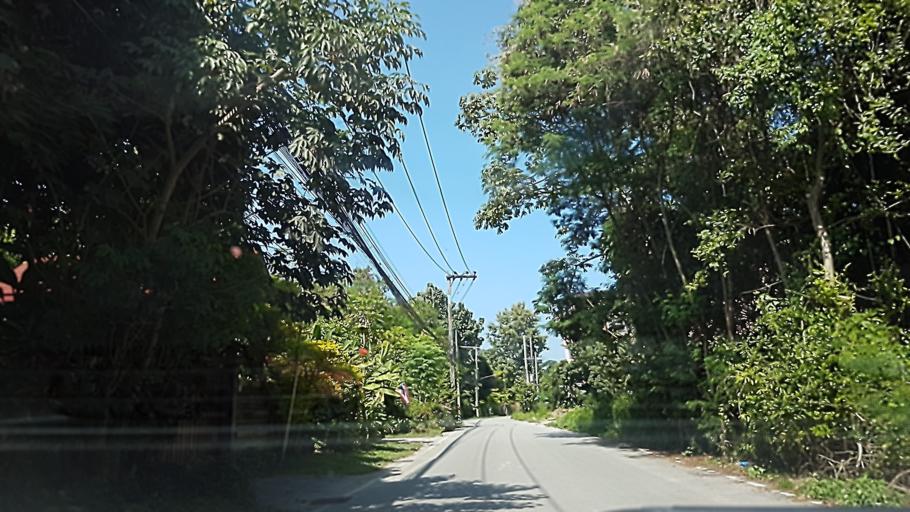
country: TH
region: Chiang Mai
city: Chiang Mai
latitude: 18.8205
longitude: 98.9573
